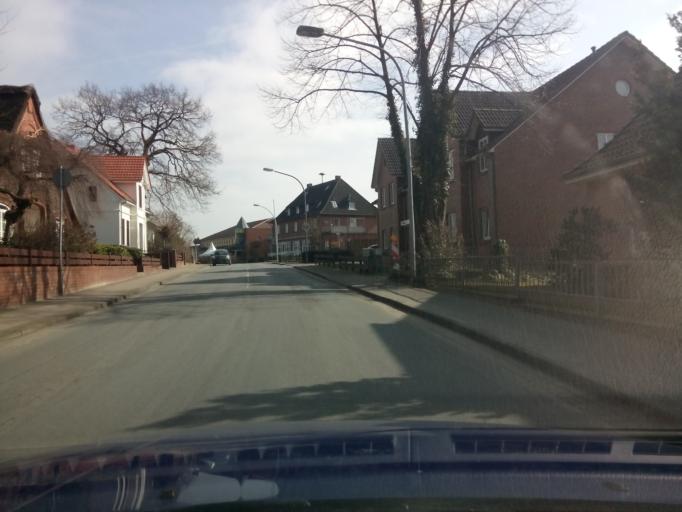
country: DE
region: Lower Saxony
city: Ritterhude
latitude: 53.1779
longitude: 8.7471
